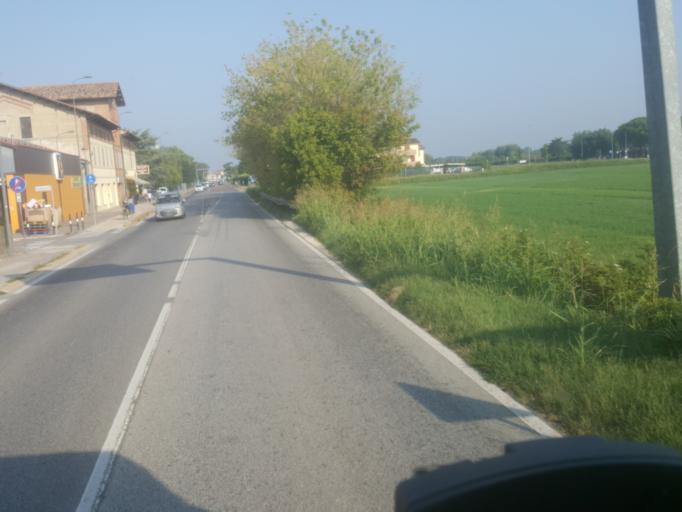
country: IT
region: Emilia-Romagna
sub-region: Provincia di Ravenna
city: Mezzano
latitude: 44.4635
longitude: 12.0924
